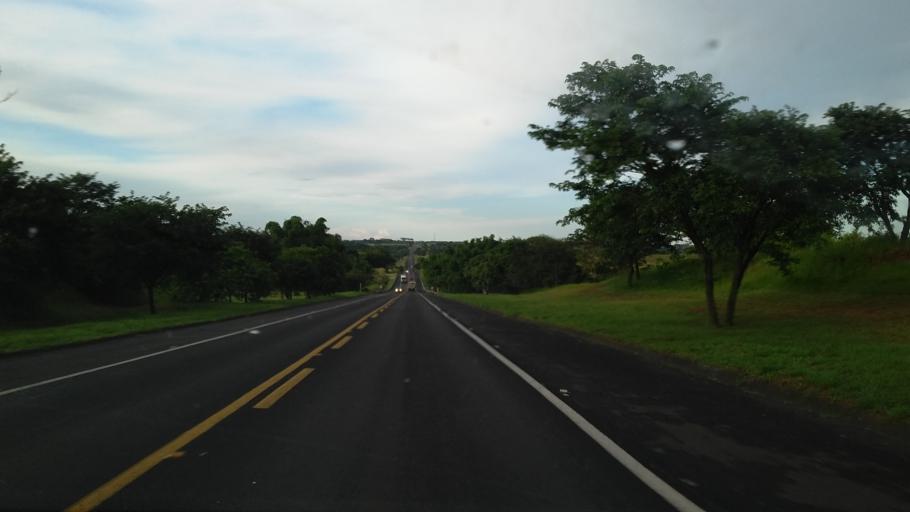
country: BR
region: Sao Paulo
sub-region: Marilia
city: Marilia
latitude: -21.9437
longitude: -49.9209
